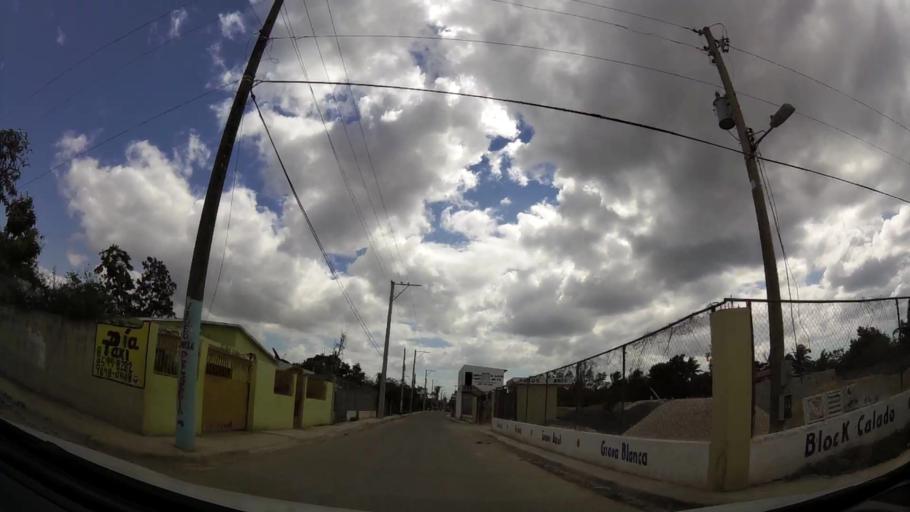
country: DO
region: Santo Domingo
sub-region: Santo Domingo
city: Boca Chica
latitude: 18.4531
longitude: -69.6472
